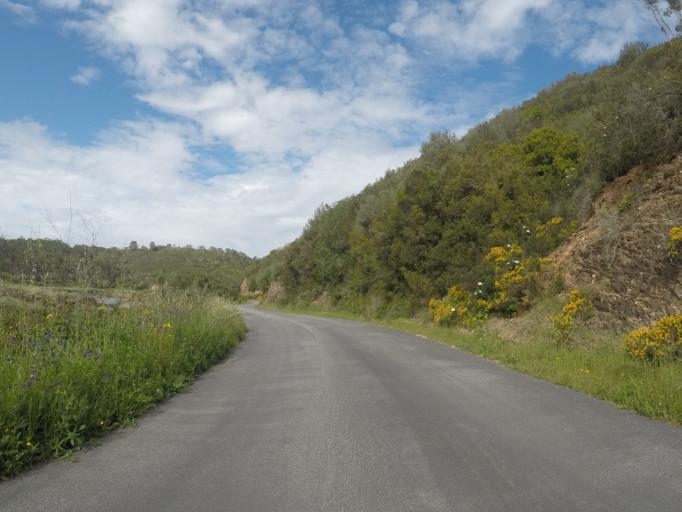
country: PT
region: Beja
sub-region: Odemira
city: Sao Teotonio
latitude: 37.4366
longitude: -8.7853
